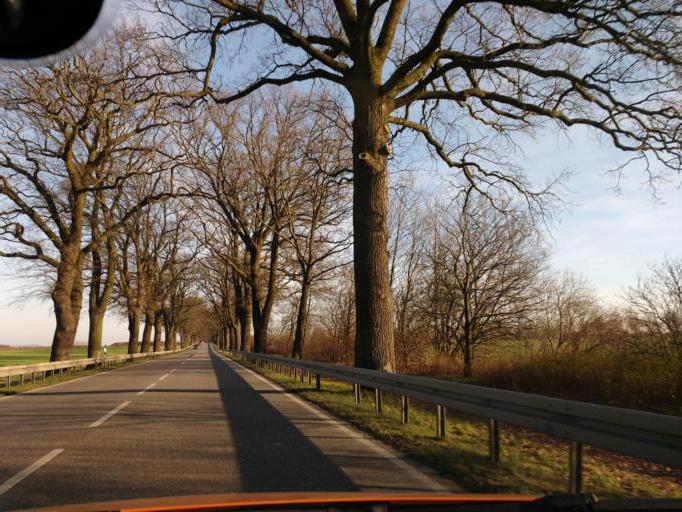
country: DE
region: Brandenburg
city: Werneuchen
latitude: 52.6271
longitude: 13.7112
